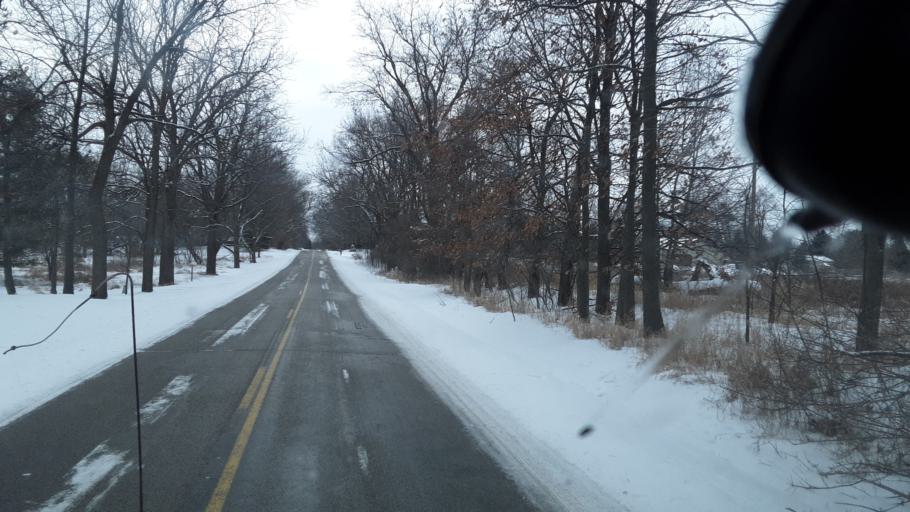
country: US
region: Michigan
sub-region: Ingham County
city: Leslie
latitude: 42.5145
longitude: -84.3889
